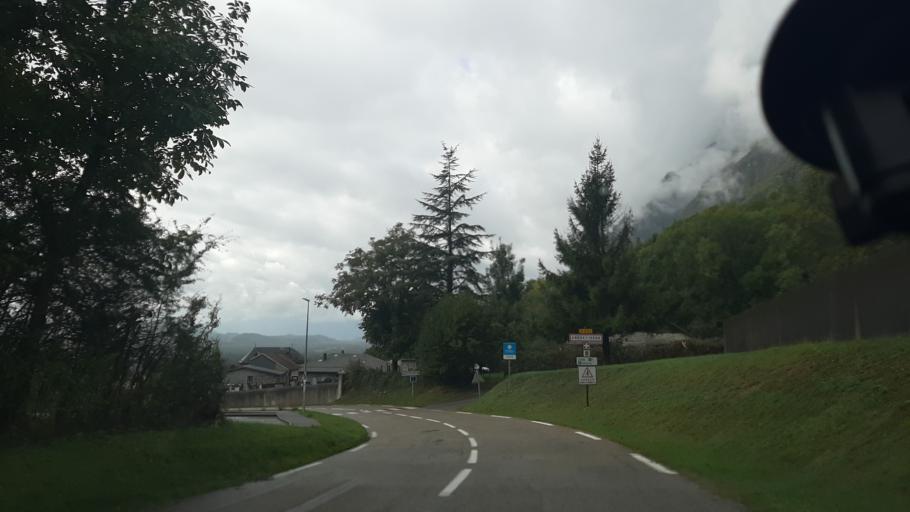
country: FR
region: Rhone-Alpes
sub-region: Departement de la Savoie
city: Gresy-sur-Isere
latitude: 45.6048
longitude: 6.2585
